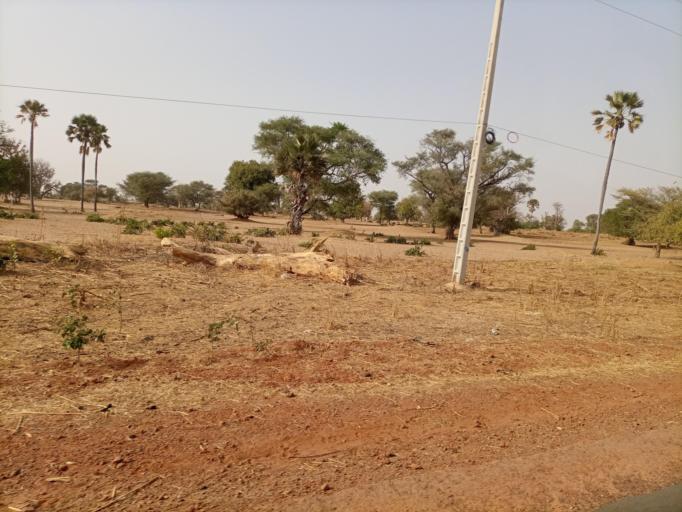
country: SN
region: Fatick
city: Foundiougne
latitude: 14.1191
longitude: -16.4461
